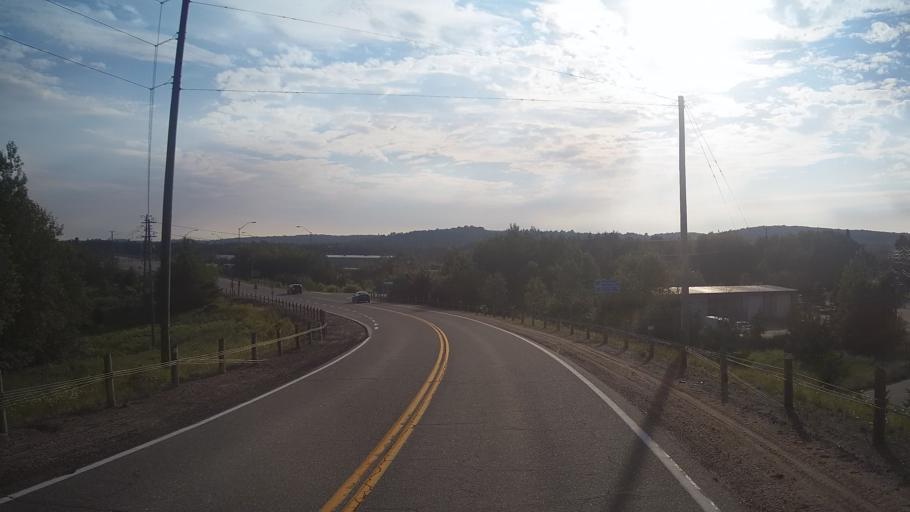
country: CA
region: Ontario
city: Huntsville
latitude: 45.3735
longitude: -79.2124
